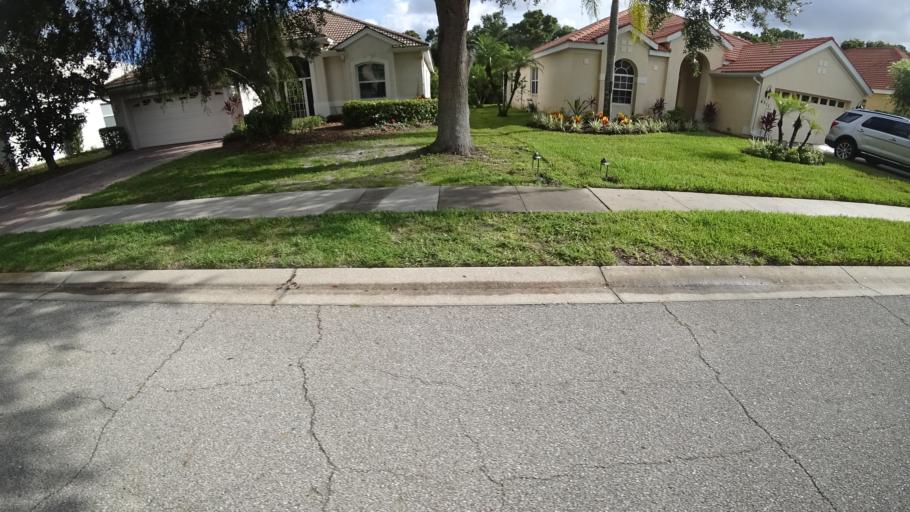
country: US
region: Florida
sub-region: Sarasota County
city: Desoto Lakes
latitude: 27.4149
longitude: -82.4768
